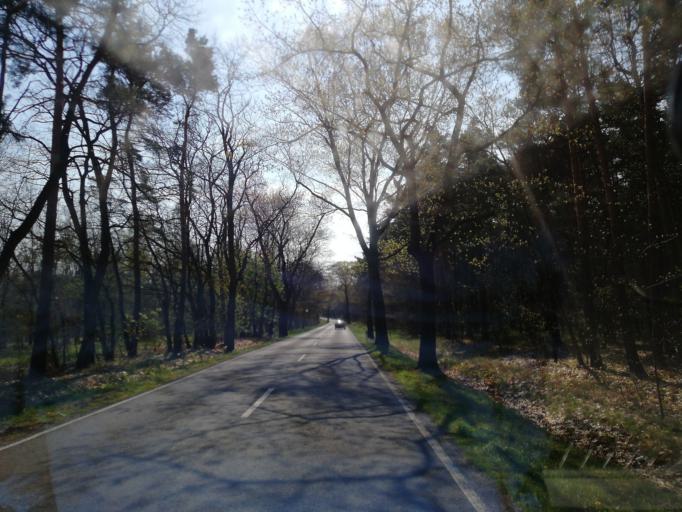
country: DE
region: Brandenburg
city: Calau
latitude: 51.7761
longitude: 13.8921
